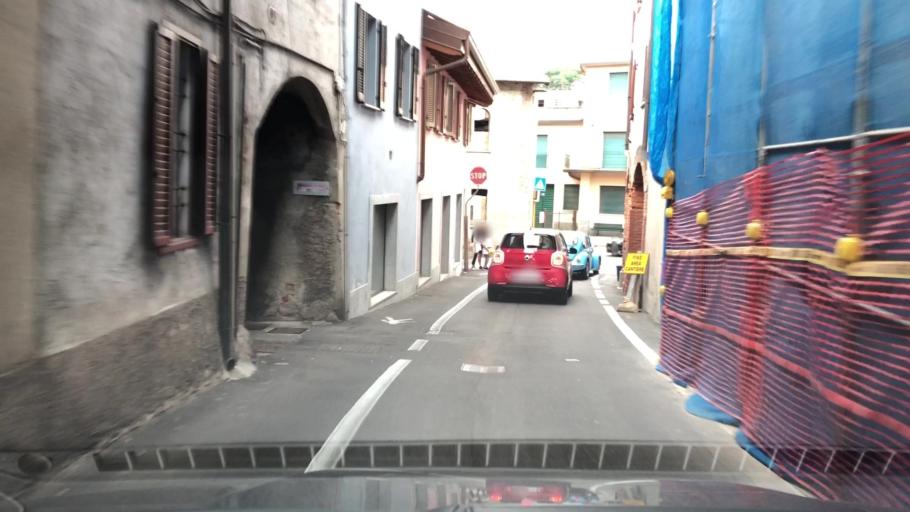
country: IT
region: Lombardy
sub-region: Provincia di Como
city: Casnate Con Bernate
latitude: 45.7562
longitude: 9.0738
